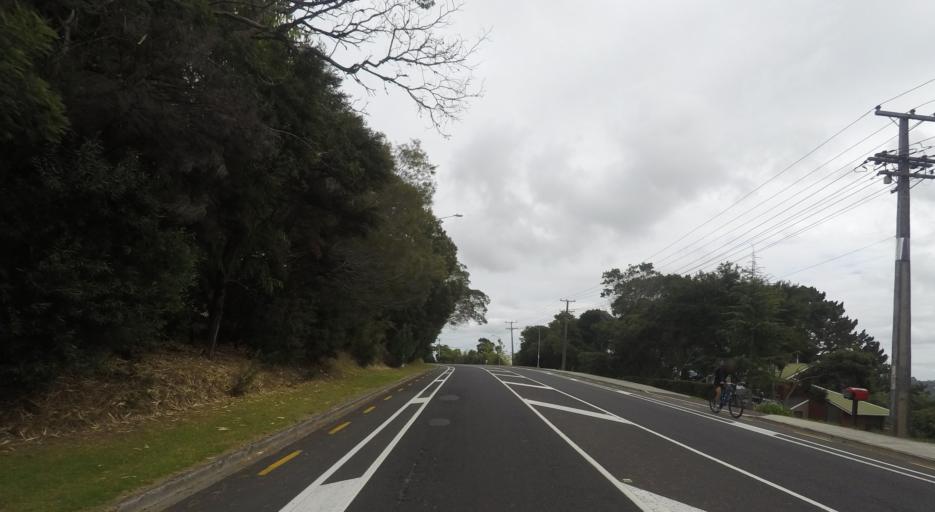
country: NZ
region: Auckland
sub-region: Auckland
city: North Shore
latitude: -36.7779
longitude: 174.6869
